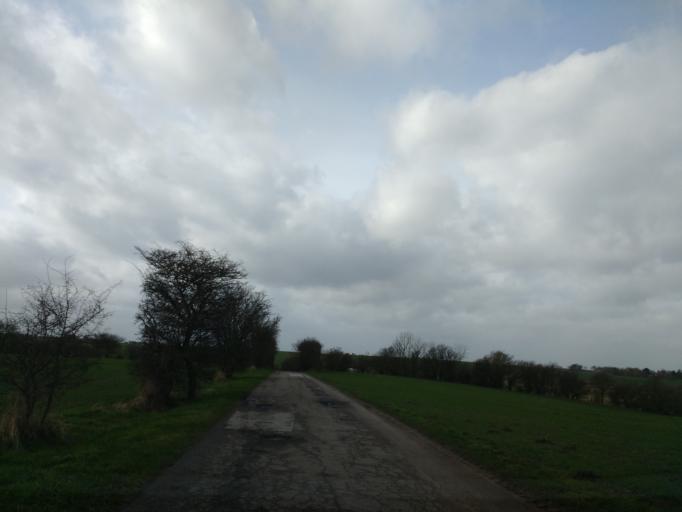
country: DE
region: Schleswig-Holstein
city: Heiligenhafen
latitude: 54.3727
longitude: 10.9446
